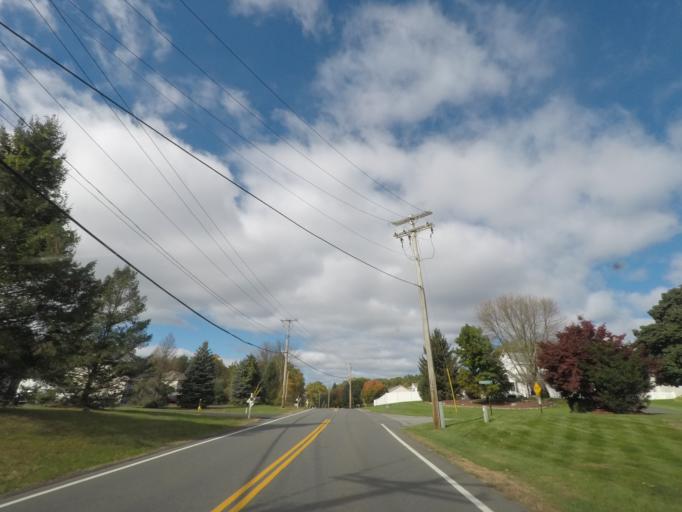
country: US
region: New York
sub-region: Albany County
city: Cohoes
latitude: 42.8289
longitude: -73.7488
